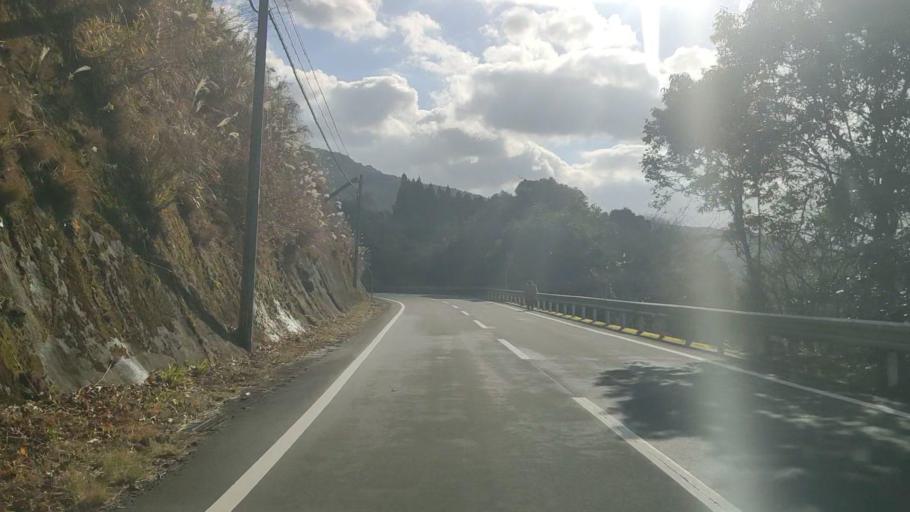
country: JP
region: Kumamoto
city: Hitoyoshi
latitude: 32.3194
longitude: 130.8421
